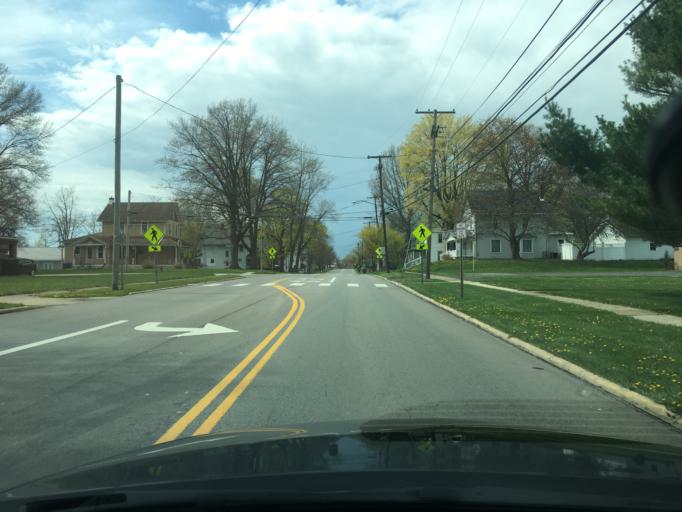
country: US
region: Ohio
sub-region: Wayne County
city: Smithville
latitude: 40.8666
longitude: -81.8544
